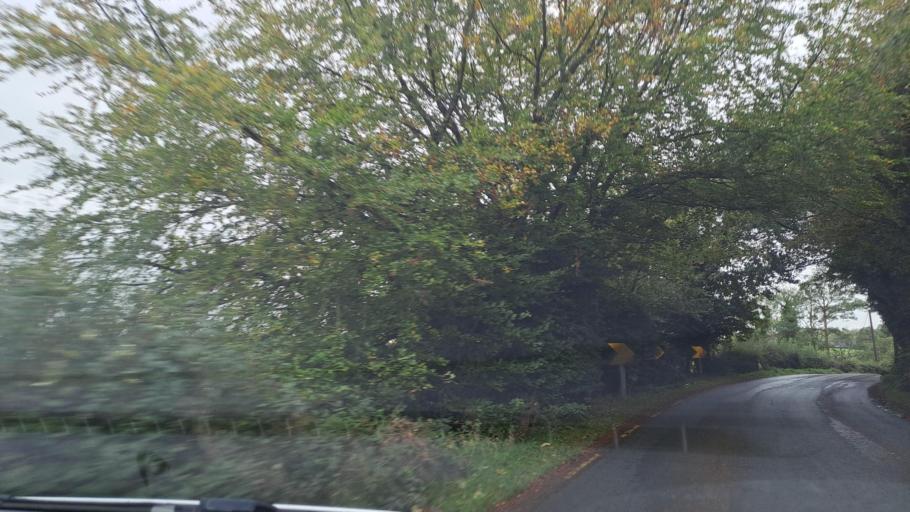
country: IE
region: Ulster
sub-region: An Cabhan
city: Cootehill
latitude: 54.0138
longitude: -7.0548
